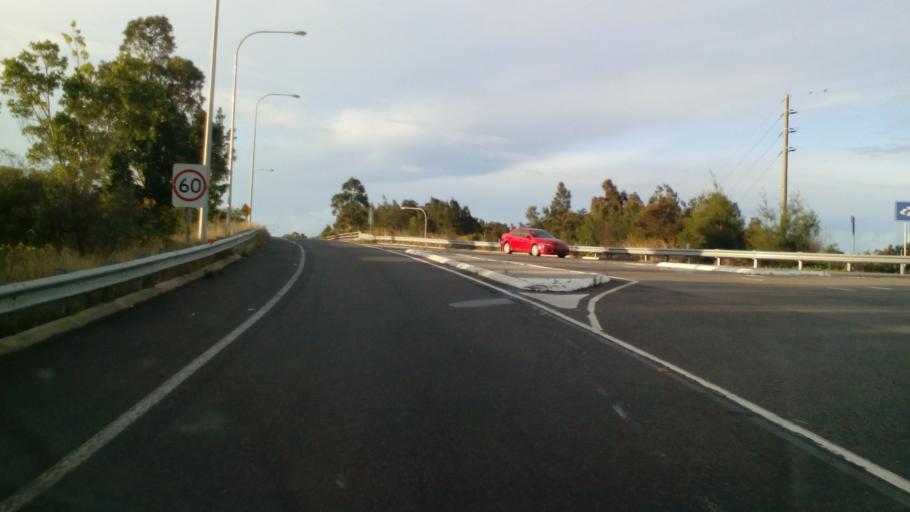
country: AU
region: New South Wales
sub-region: Newcastle
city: Beresfield
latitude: -32.8129
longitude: 151.6654
